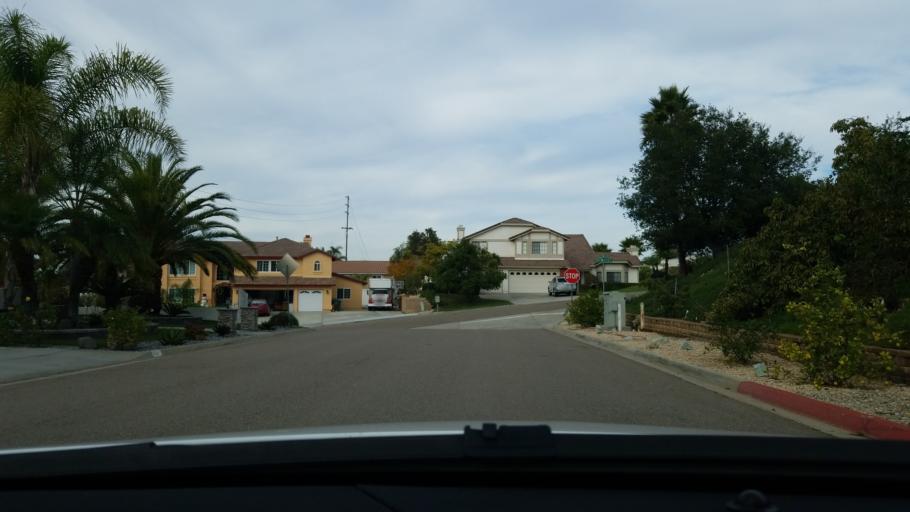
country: US
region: California
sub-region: San Diego County
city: Casa de Oro-Mount Helix
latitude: 32.7727
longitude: -116.9575
